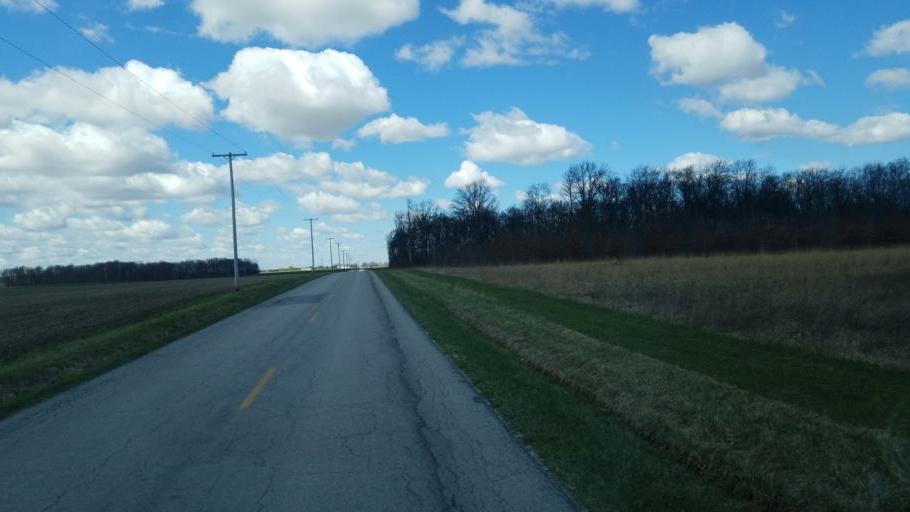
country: US
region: Ohio
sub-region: Sandusky County
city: Mount Carmel
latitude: 41.2418
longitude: -82.9778
